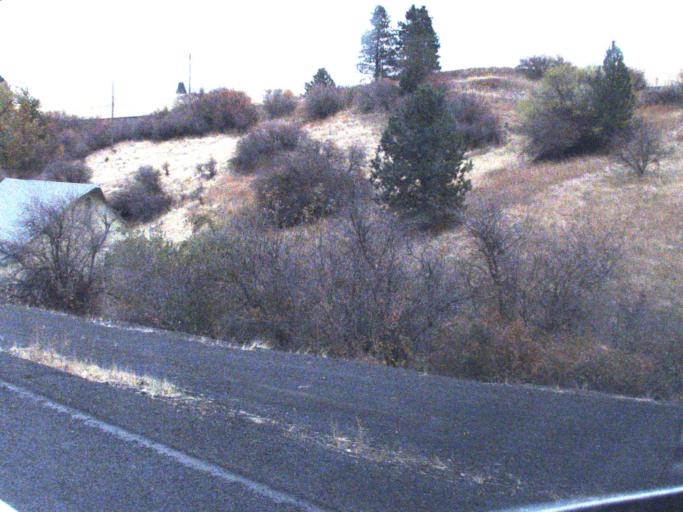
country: US
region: Washington
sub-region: Whitman County
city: Colfax
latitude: 46.8873
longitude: -117.3869
